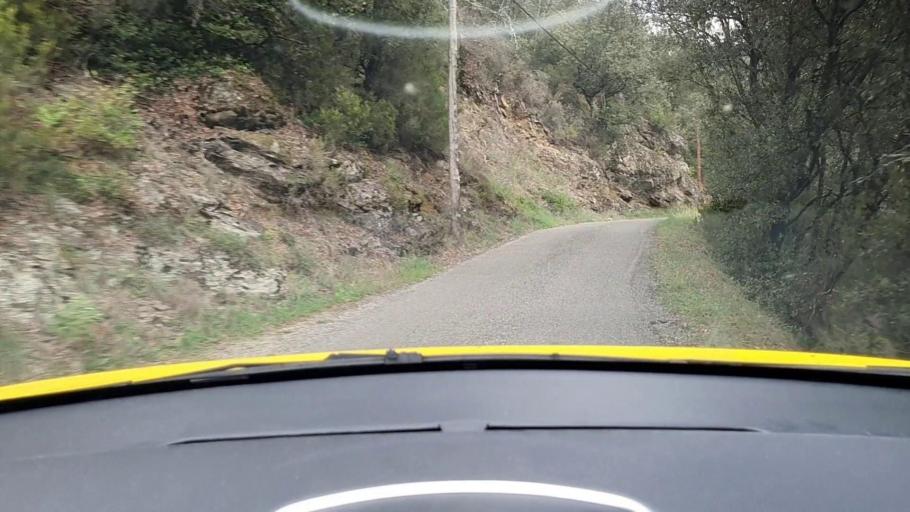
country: FR
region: Languedoc-Roussillon
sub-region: Departement du Gard
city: Sumene
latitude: 44.0137
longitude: 3.6607
